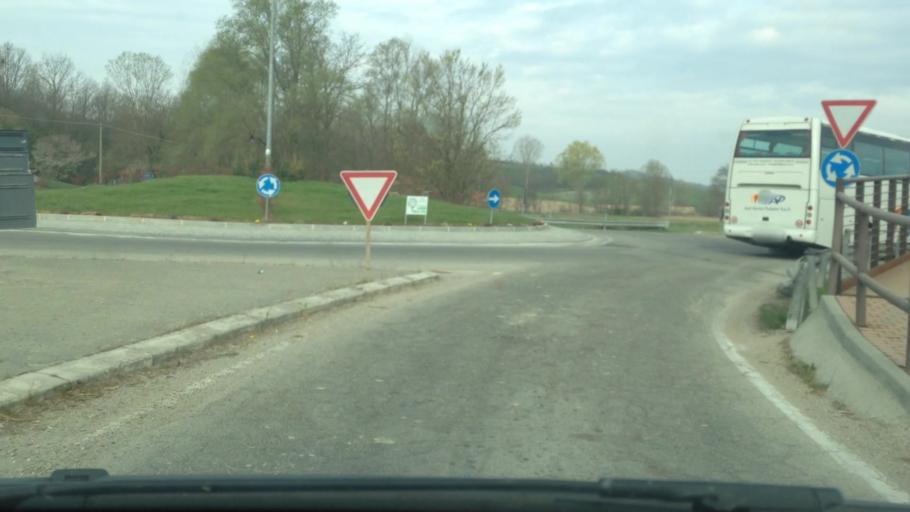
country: IT
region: Piedmont
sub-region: Provincia di Asti
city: San Damiano d'Asti
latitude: 44.8454
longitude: 8.0716
